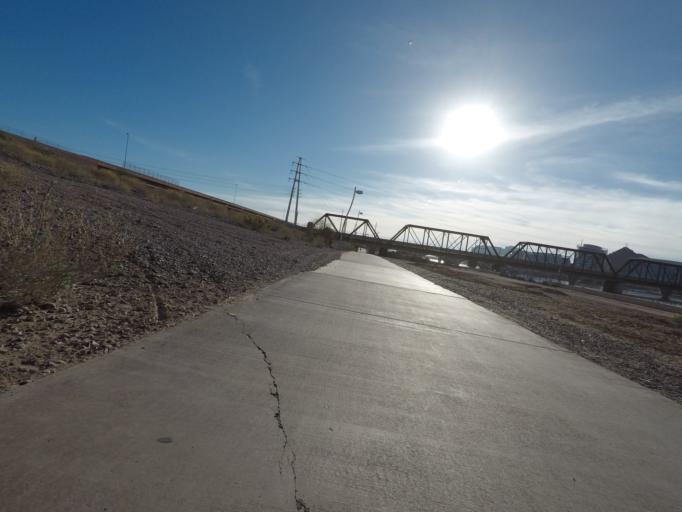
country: US
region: Arizona
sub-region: Maricopa County
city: Tempe Junction
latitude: 33.4348
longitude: -111.9454
